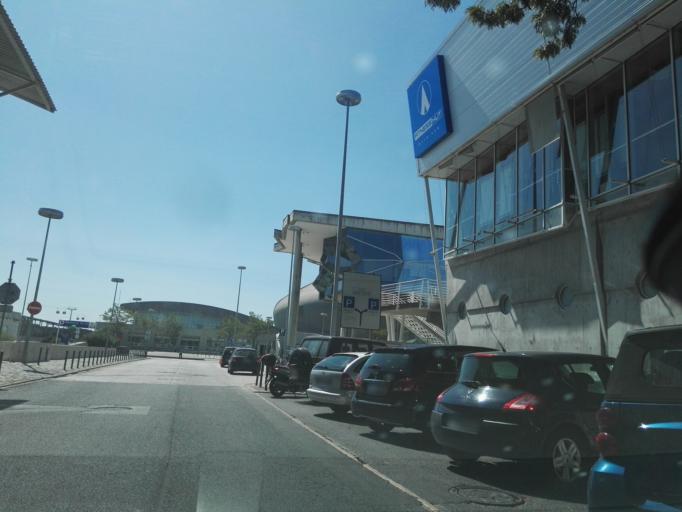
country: PT
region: Lisbon
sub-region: Loures
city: Moscavide
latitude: 38.7702
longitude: -9.0927
